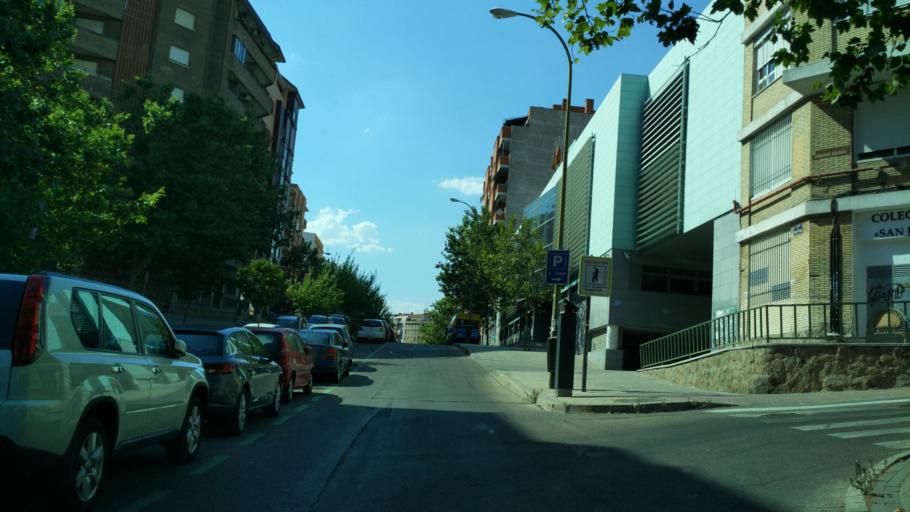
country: ES
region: Madrid
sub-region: Provincia de Madrid
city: Tetuan de las Victorias
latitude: 40.4541
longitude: -3.7048
